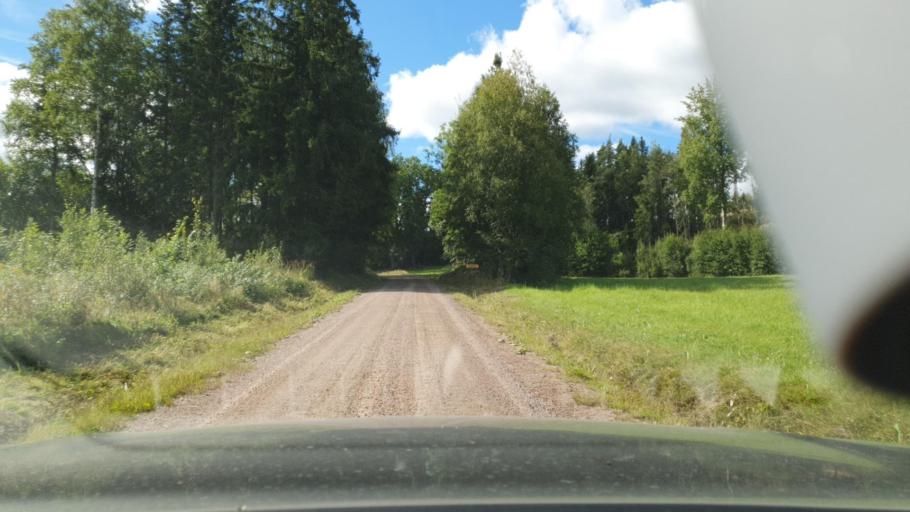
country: SE
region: Vaermland
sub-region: Storfors Kommun
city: Storfors
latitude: 59.5419
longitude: 14.0862
